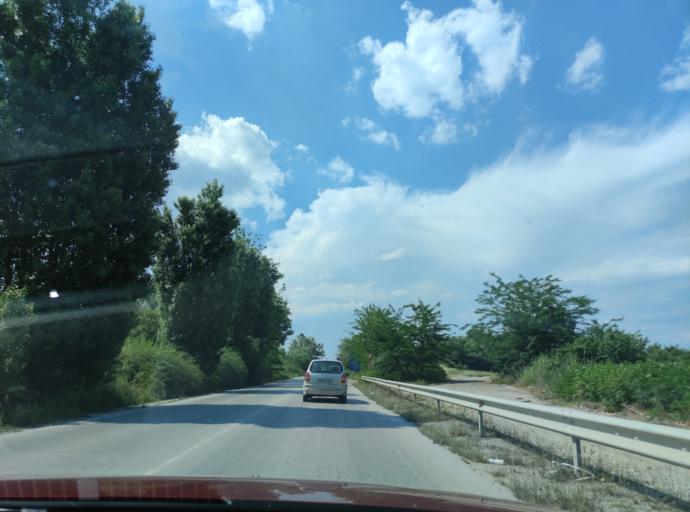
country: BG
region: Plovdiv
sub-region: Obshtina Plovdiv
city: Plovdiv
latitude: 42.1190
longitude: 24.6769
